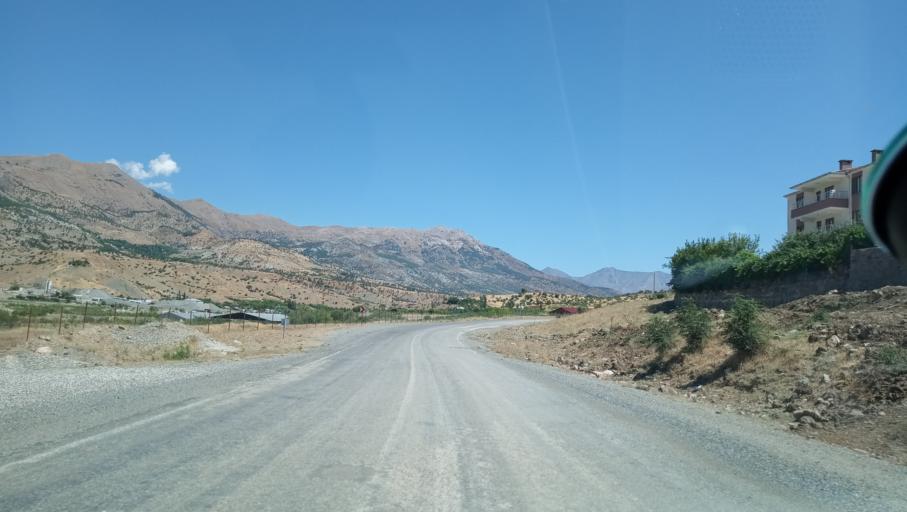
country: TR
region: Diyarbakir
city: Kulp
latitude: 38.4934
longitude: 41.0444
